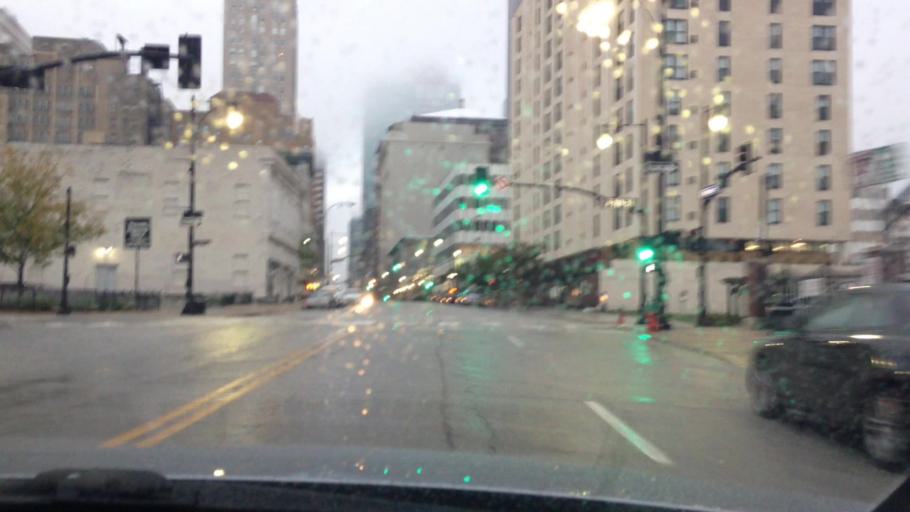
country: US
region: Missouri
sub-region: Jackson County
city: Kansas City
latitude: 39.1058
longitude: -94.5817
